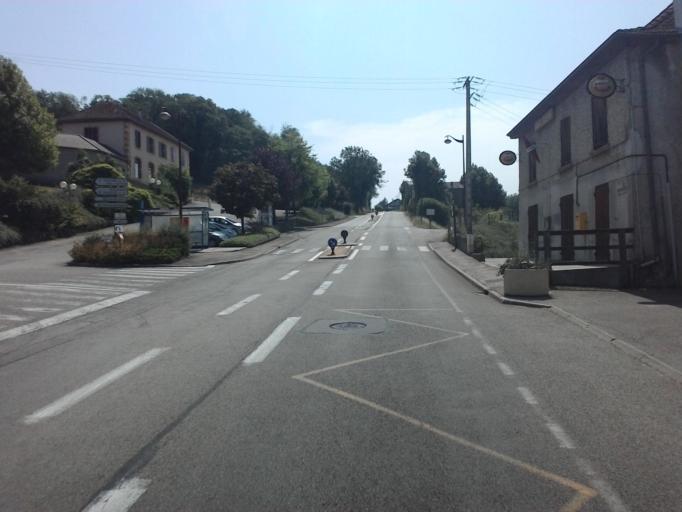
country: FR
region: Rhone-Alpes
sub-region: Departement de l'Isere
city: Montferrat
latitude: 45.5096
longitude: 5.5969
